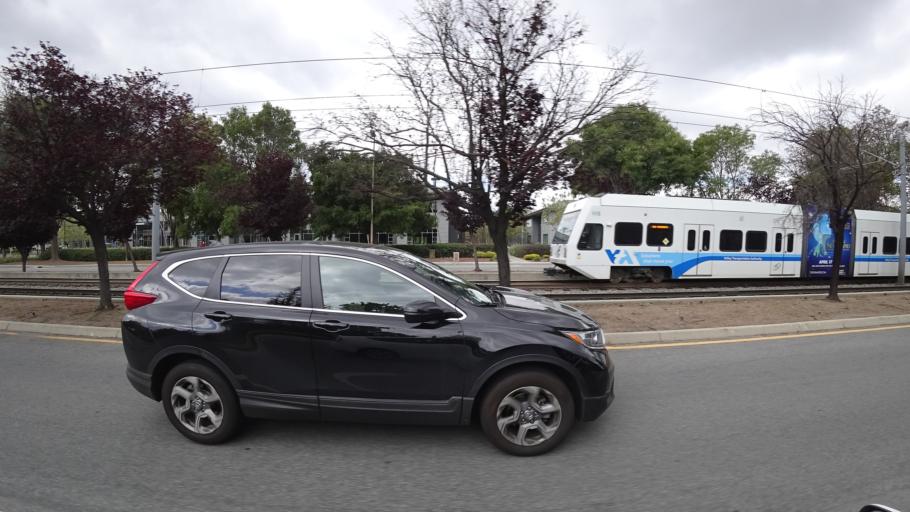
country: US
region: California
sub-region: Santa Clara County
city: Milpitas
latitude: 37.4085
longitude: -121.9510
